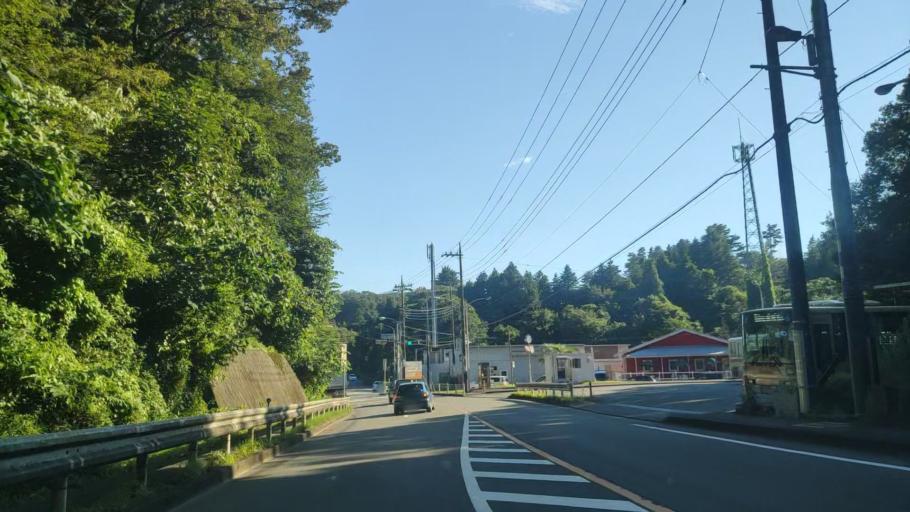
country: JP
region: Tokyo
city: Hachioji
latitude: 35.6123
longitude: 139.3114
